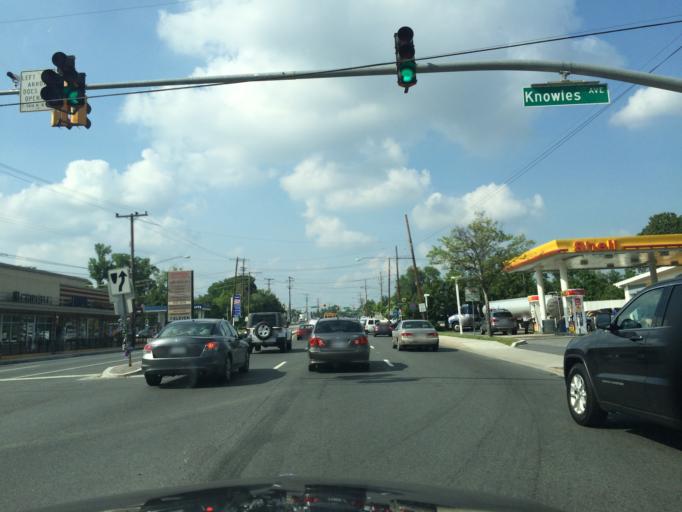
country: US
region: Maryland
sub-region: Montgomery County
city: Kensington
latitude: 39.0275
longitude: -77.0765
